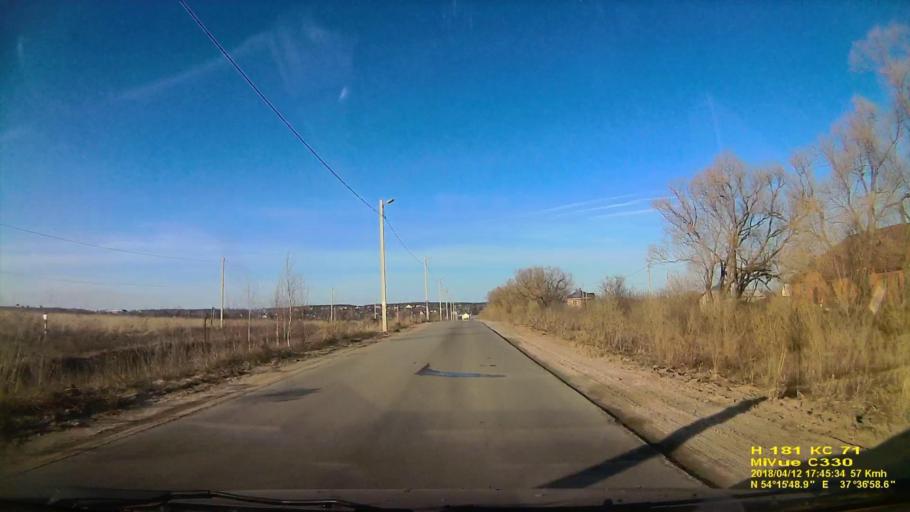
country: RU
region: Tula
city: Gorelki
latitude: 54.2637
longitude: 37.6164
